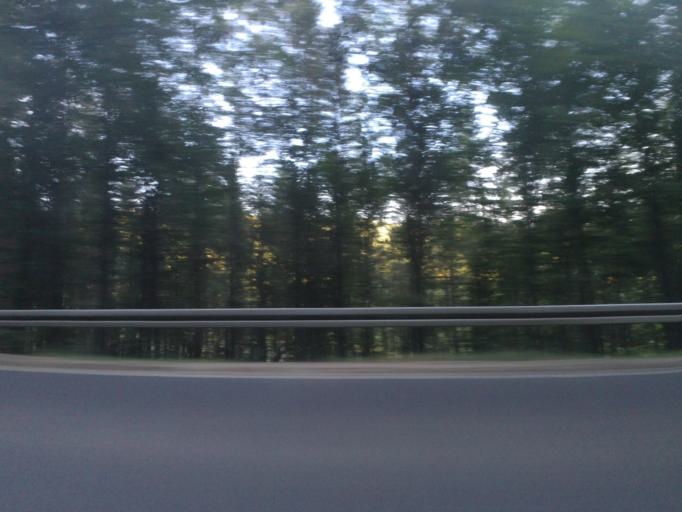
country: DE
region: Hesse
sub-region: Regierungsbezirk Darmstadt
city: Gelnhausen
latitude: 50.2577
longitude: 9.2078
